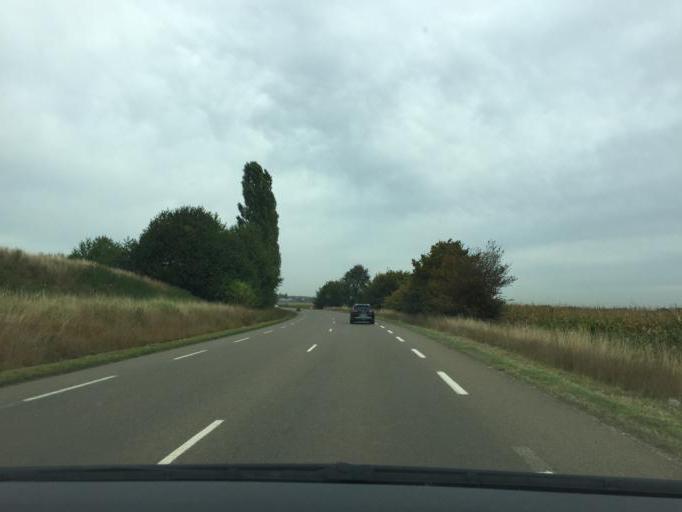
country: FR
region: Ile-de-France
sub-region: Departement de l'Essonne
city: Villiers-le-Bacle
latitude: 48.7449
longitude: 2.1222
